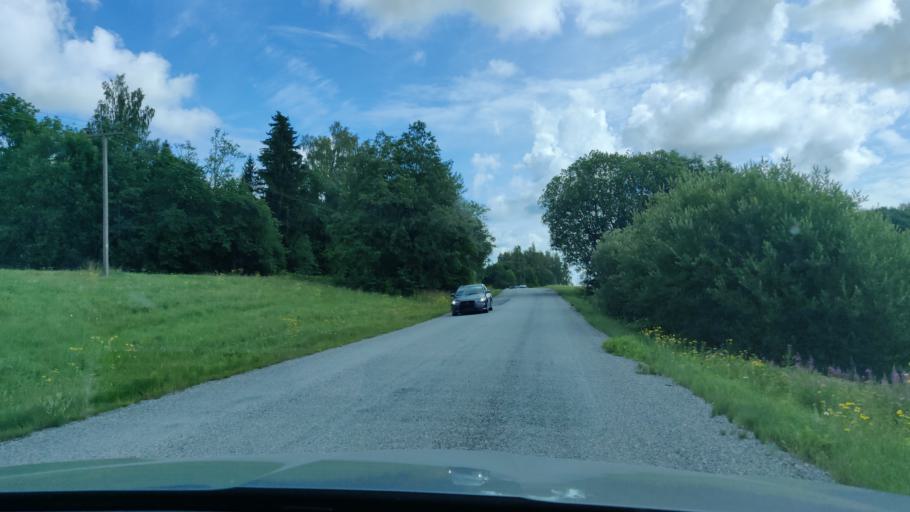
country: EE
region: Tartu
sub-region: Elva linn
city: Elva
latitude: 58.0242
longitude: 26.3384
